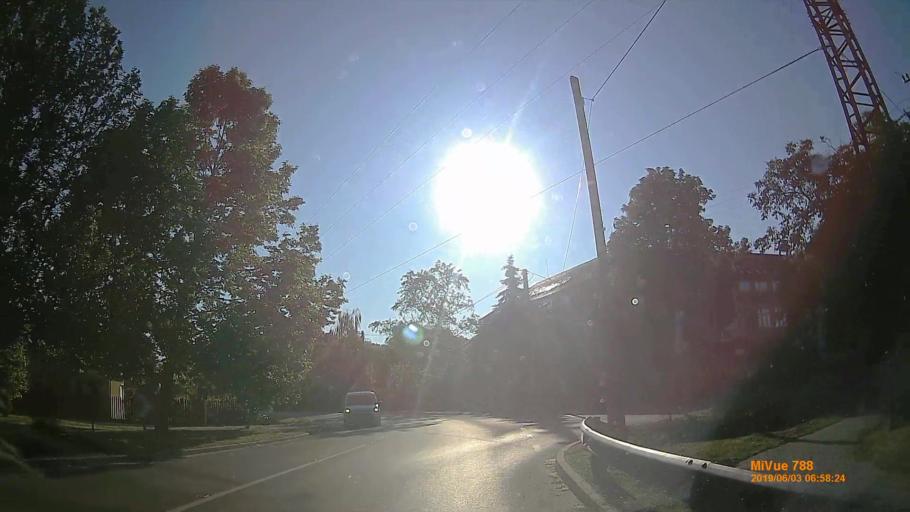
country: HU
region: Pest
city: Dabas
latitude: 47.2167
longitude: 19.2736
